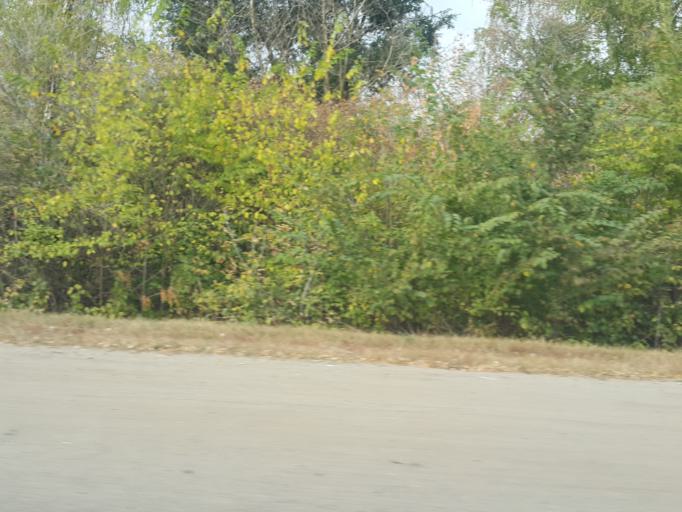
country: RU
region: Tambov
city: Bokino
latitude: 52.6653
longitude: 41.4501
